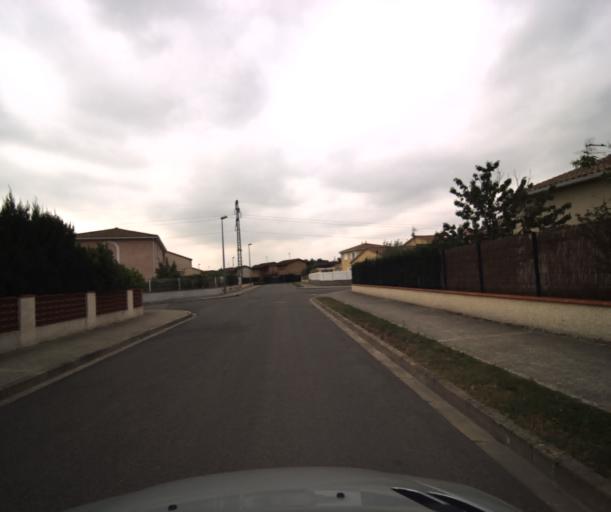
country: FR
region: Midi-Pyrenees
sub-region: Departement de la Haute-Garonne
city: Portet-sur-Garonne
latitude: 43.5364
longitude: 1.4143
